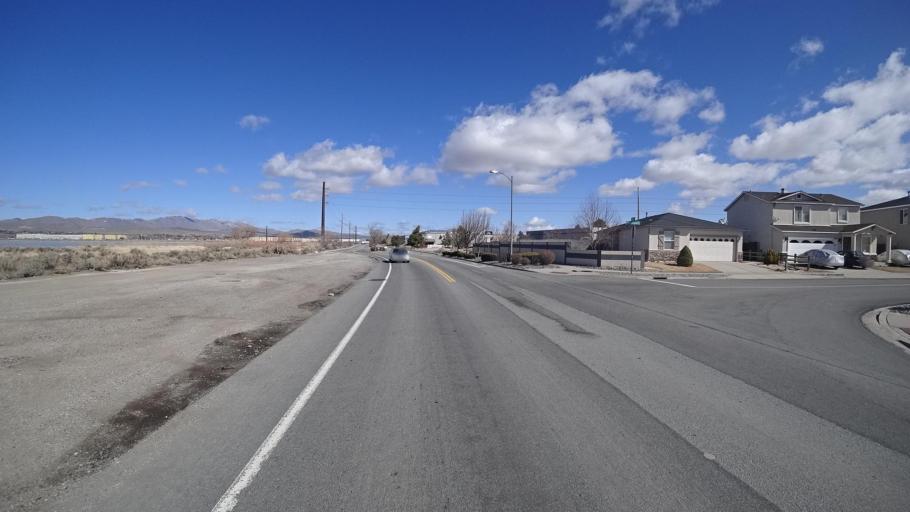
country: US
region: Nevada
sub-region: Washoe County
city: Lemmon Valley
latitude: 39.6386
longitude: -119.8971
